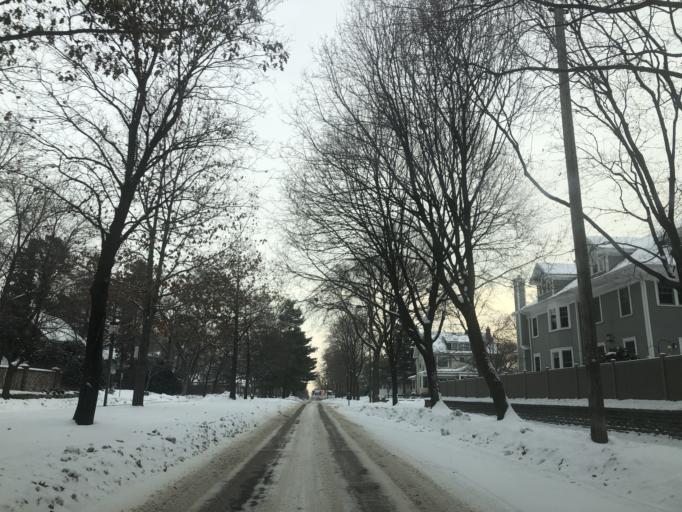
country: US
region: Minnesota
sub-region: Hennepin County
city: Richfield
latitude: 44.9196
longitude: -93.2955
